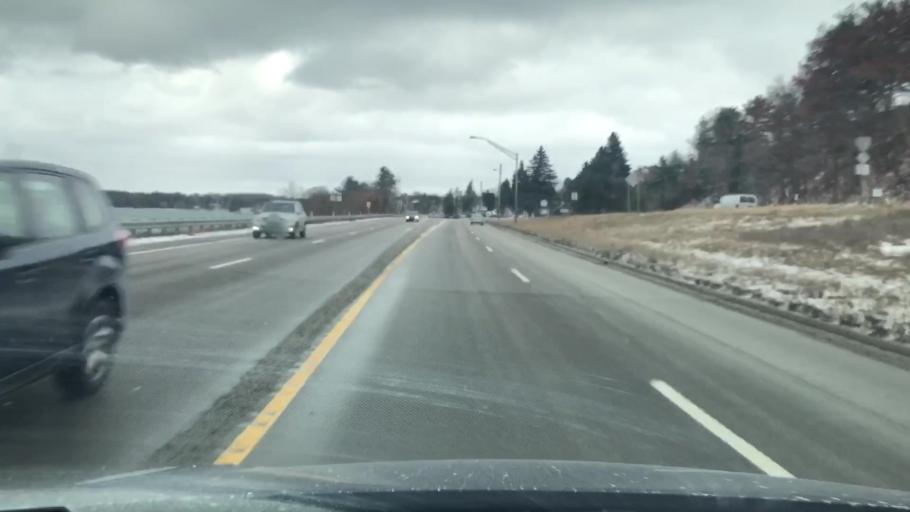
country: US
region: Michigan
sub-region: Grand Traverse County
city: Traverse City
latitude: 44.7607
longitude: -85.5136
